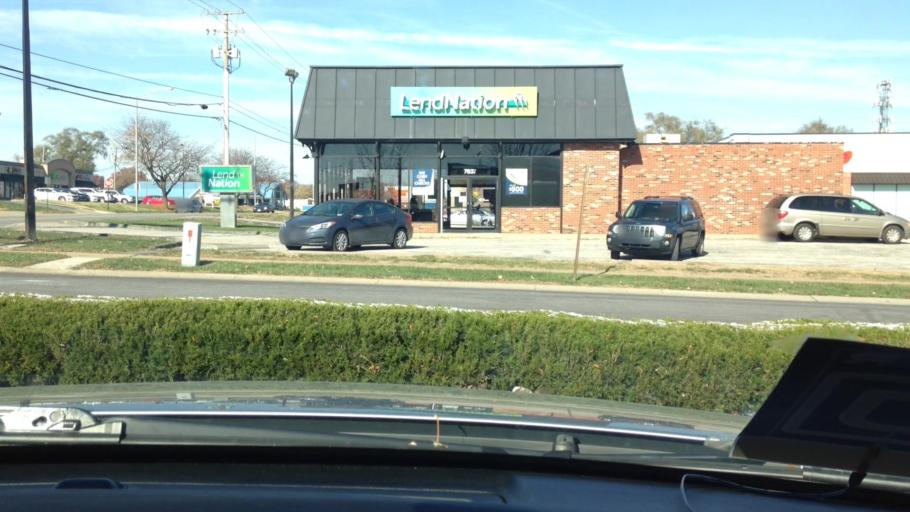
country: US
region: Kansas
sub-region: Johnson County
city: Overland Park
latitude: 38.9894
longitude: -94.6674
